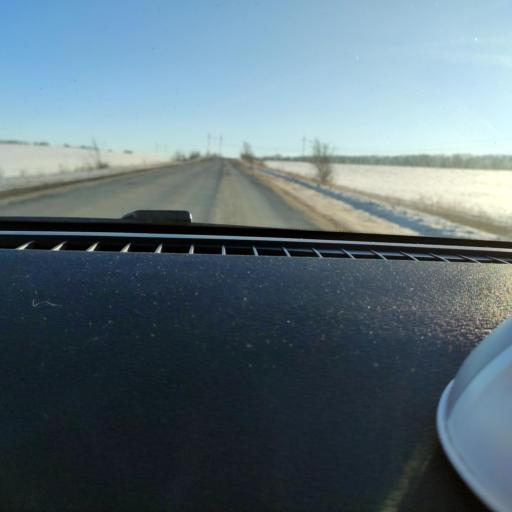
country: RU
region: Samara
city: Kinel'
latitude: 53.1467
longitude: 50.5169
